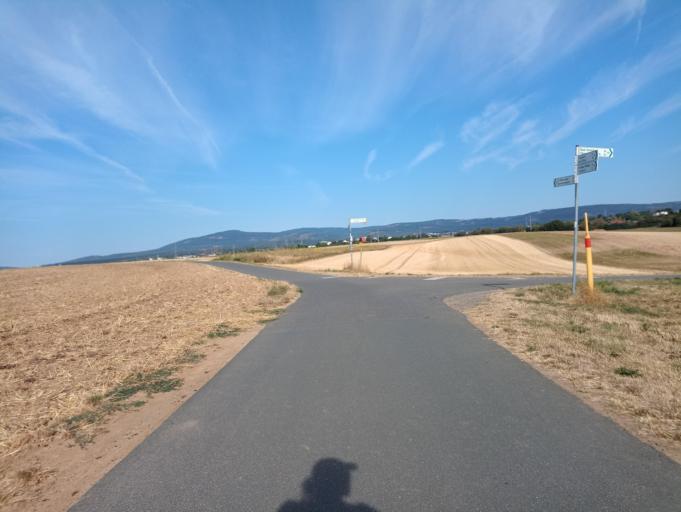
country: DE
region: Hesse
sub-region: Regierungsbezirk Darmstadt
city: Bad Homburg vor der Hoehe
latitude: 50.1892
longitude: 8.6227
